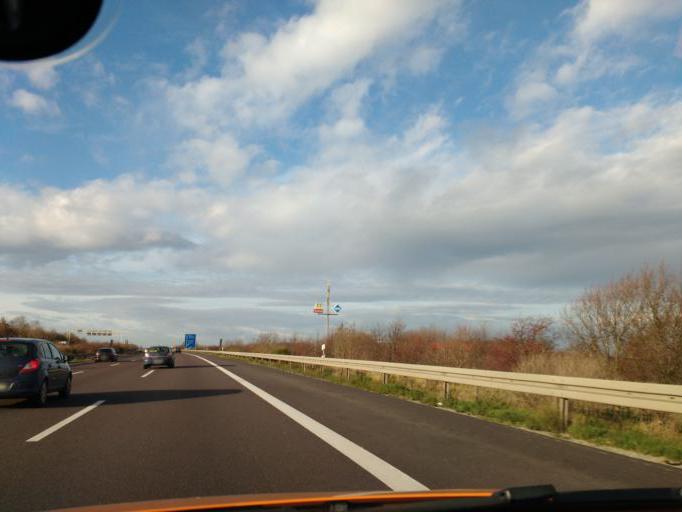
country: DE
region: Lower Saxony
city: Konigslutter am Elm
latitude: 52.3098
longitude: 10.8290
